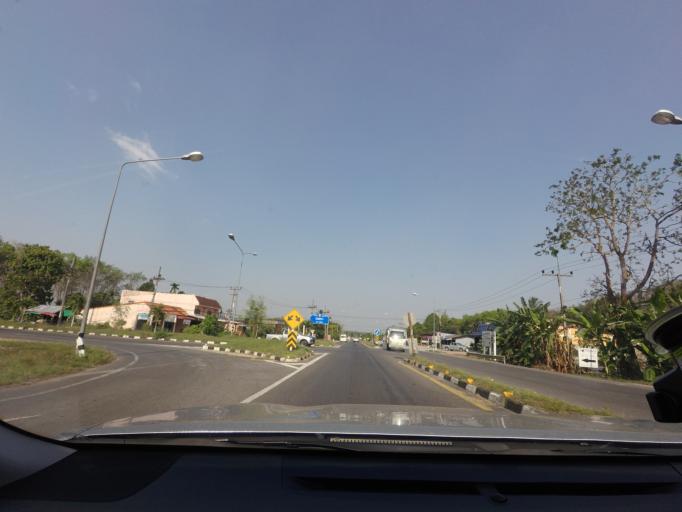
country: TH
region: Surat Thani
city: Phrasaeng
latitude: 8.5719
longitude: 99.2050
